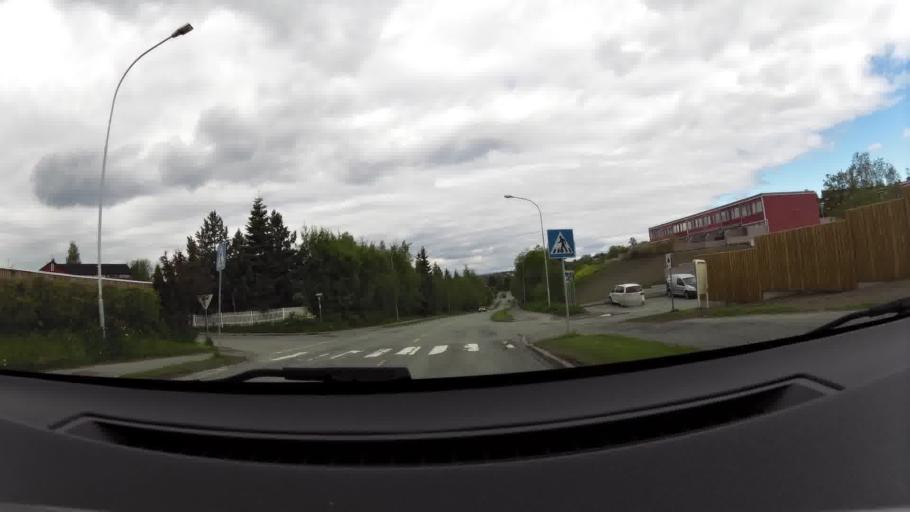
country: NO
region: Sor-Trondelag
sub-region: Trondheim
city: Trondheim
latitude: 63.3971
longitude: 10.4220
